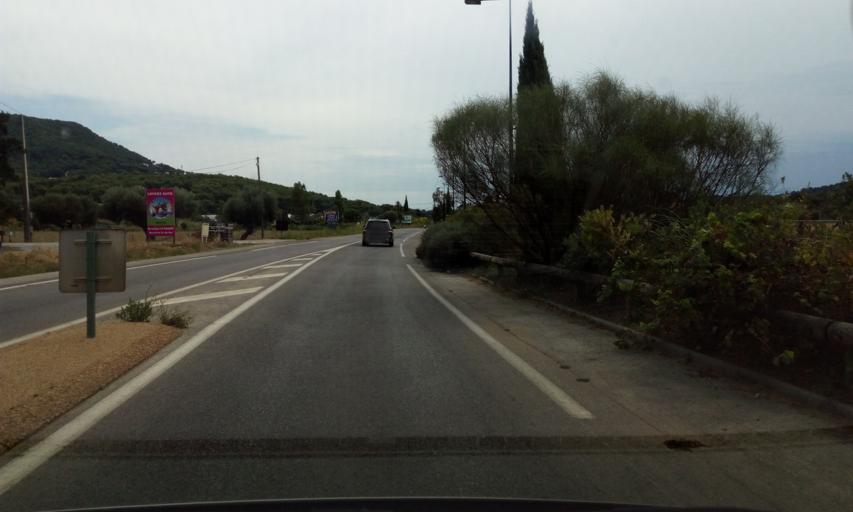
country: FR
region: Provence-Alpes-Cote d'Azur
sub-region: Departement du Var
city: Carqueiranne
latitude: 43.1078
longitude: 6.0491
